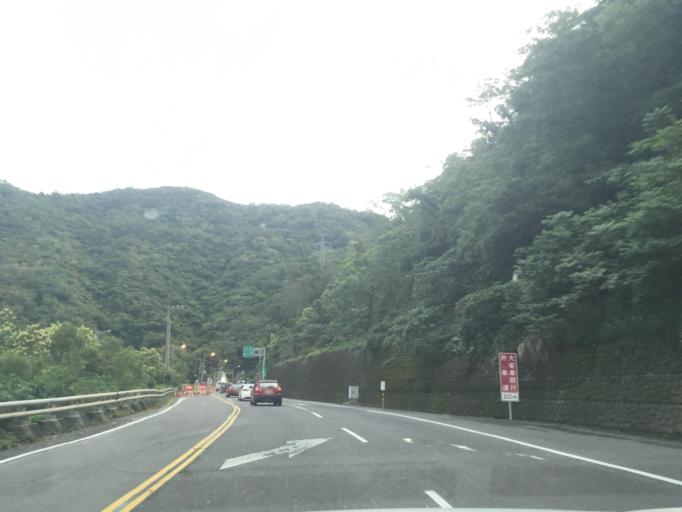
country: TW
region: Taiwan
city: Hengchun
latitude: 22.2365
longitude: 120.8033
